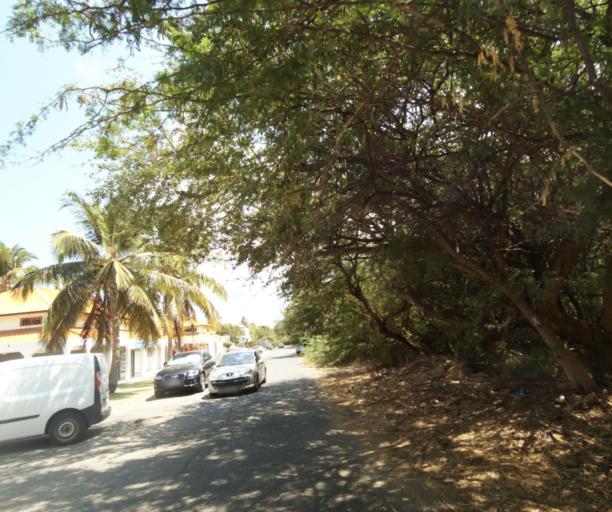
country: RE
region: Reunion
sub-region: Reunion
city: Trois-Bassins
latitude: -21.0877
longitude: 55.2332
